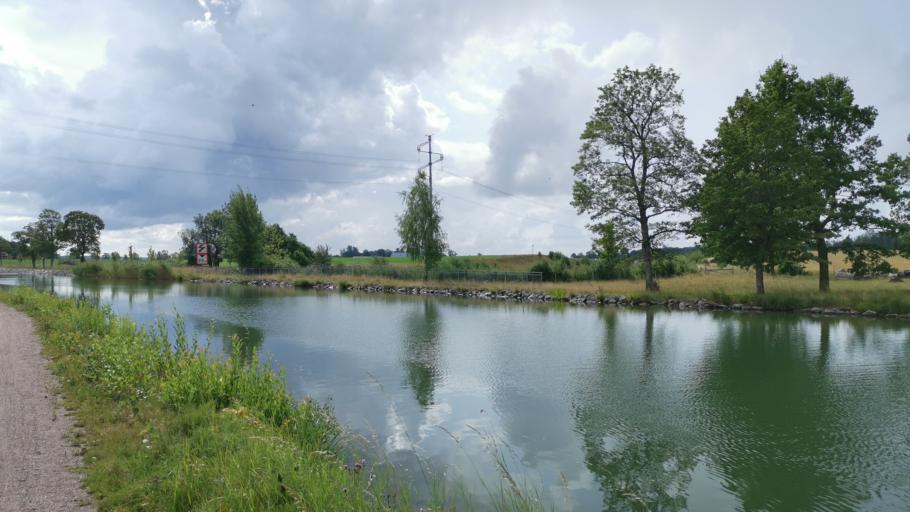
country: SE
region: OEstergoetland
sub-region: Motala Kommun
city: Borensberg
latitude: 58.5510
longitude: 15.3209
